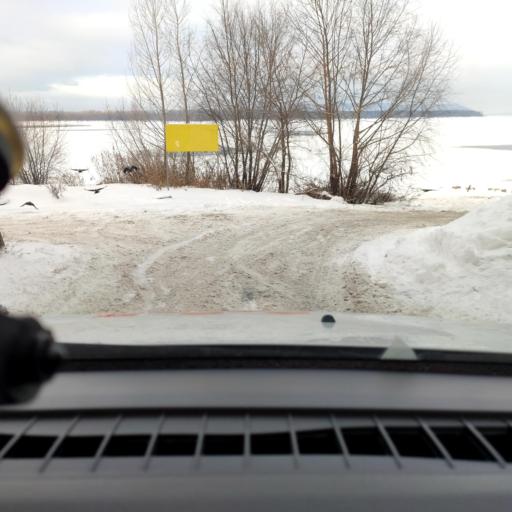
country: RU
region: Samara
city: Samara
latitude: 53.2805
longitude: 50.1887
